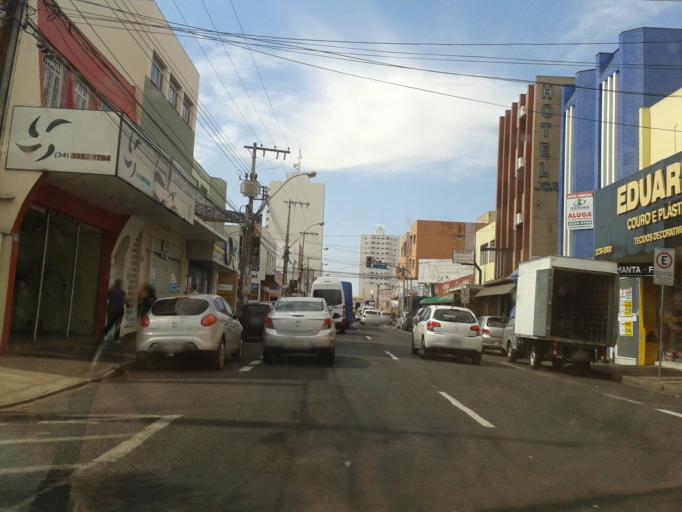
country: BR
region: Minas Gerais
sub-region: Uberlandia
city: Uberlandia
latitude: -18.9124
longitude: -48.2736
